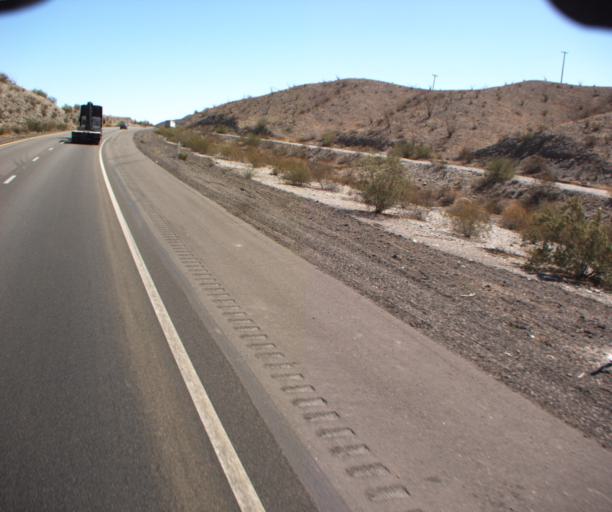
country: US
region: Arizona
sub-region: Yuma County
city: Fortuna Foothills
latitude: 32.6605
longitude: -114.3546
